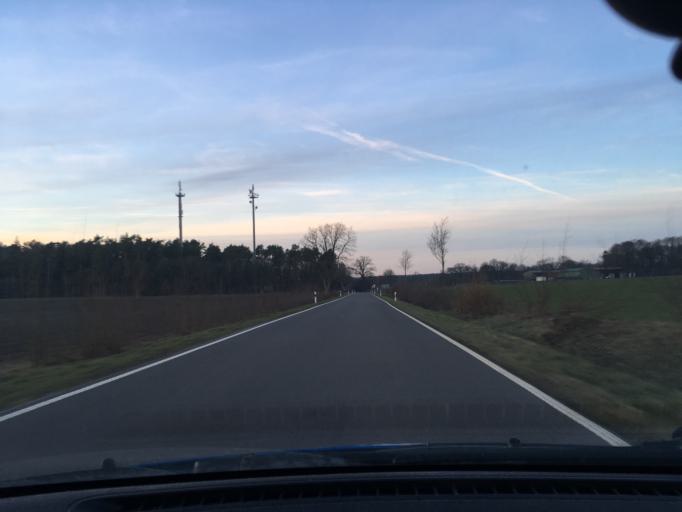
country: DE
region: Schleswig-Holstein
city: Besenthal
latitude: 53.5390
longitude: 10.7397
